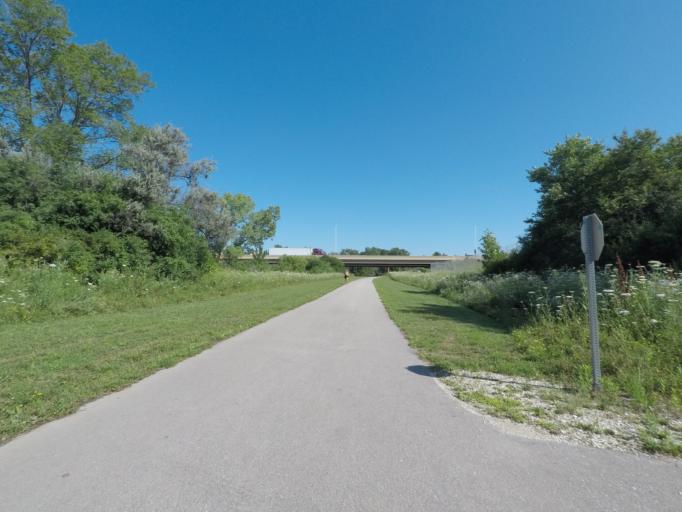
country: US
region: Wisconsin
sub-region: Waukesha County
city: Elm Grove
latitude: 43.0284
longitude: -88.0662
